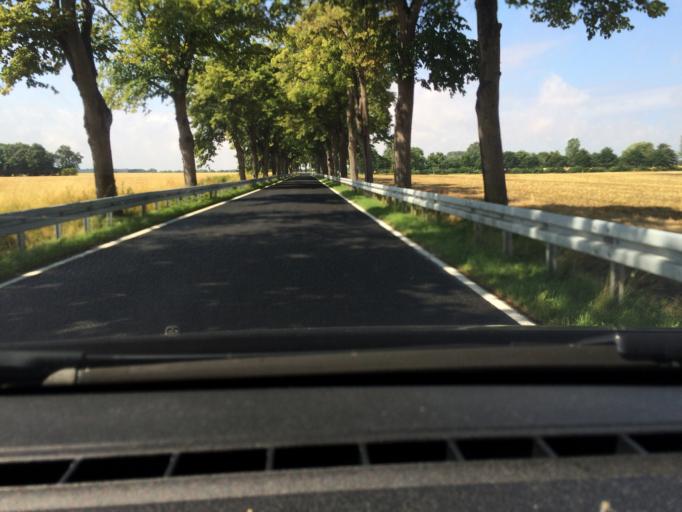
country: DE
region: Mecklenburg-Vorpommern
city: Niepars
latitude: 54.3329
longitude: 12.8686
